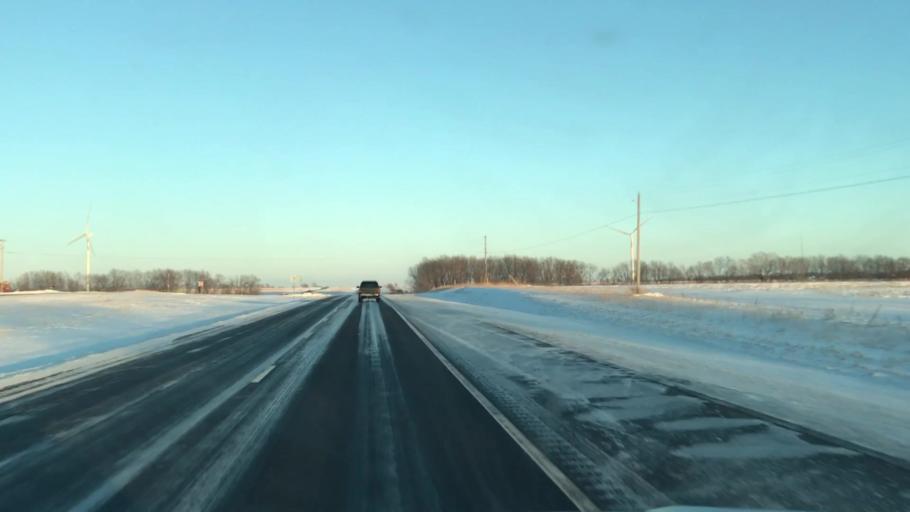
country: US
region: Missouri
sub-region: DeKalb County
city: Maysville
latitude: 39.7614
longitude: -94.3898
